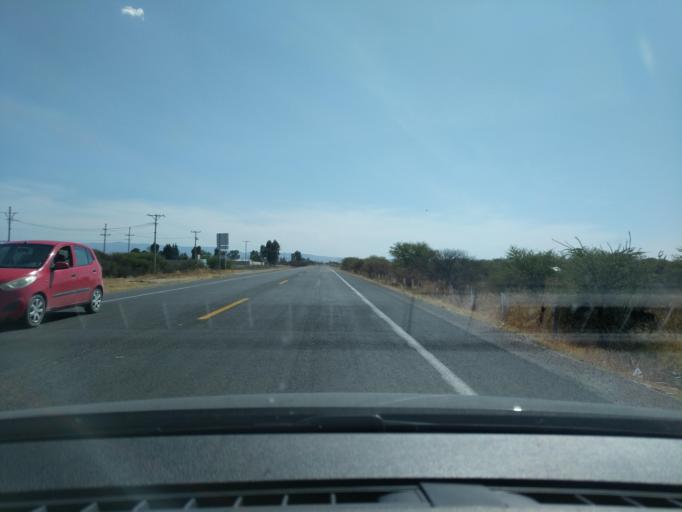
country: MX
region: Durango
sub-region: Durango
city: Jose Refugio Salcido
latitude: 24.0120
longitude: -104.5262
